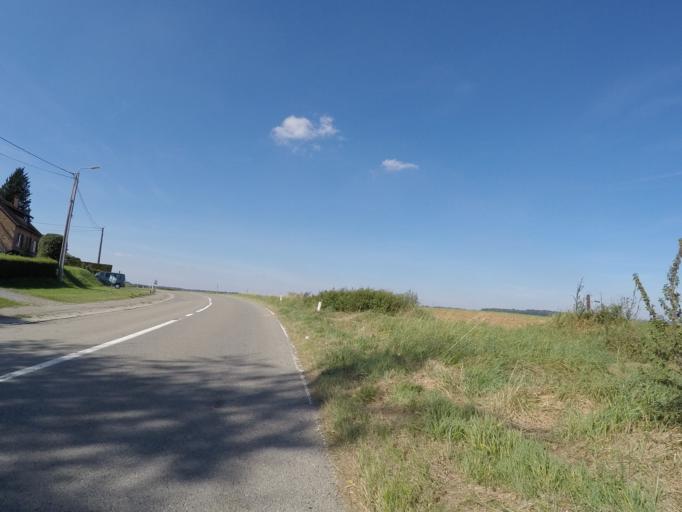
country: BE
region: Wallonia
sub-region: Province de Namur
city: Ciney
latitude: 50.3125
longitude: 5.0532
